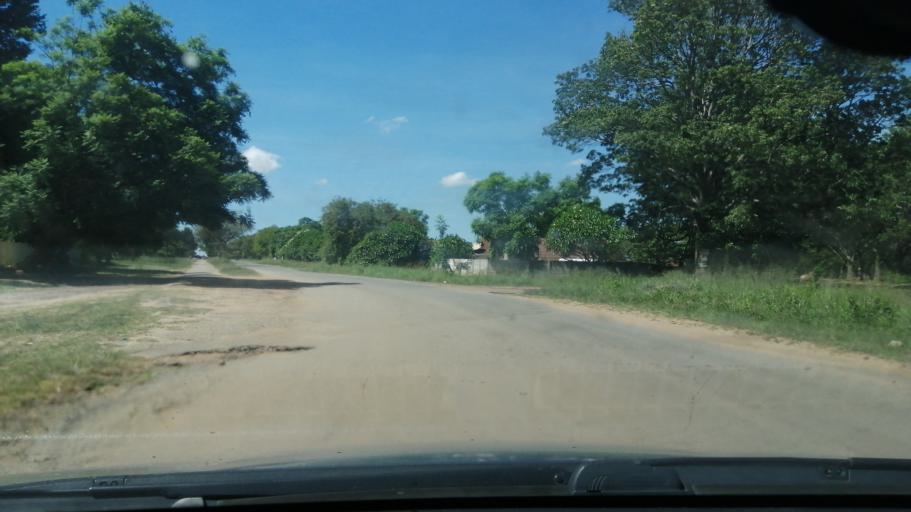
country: ZW
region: Harare
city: Epworth
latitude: -17.8225
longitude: 31.1263
